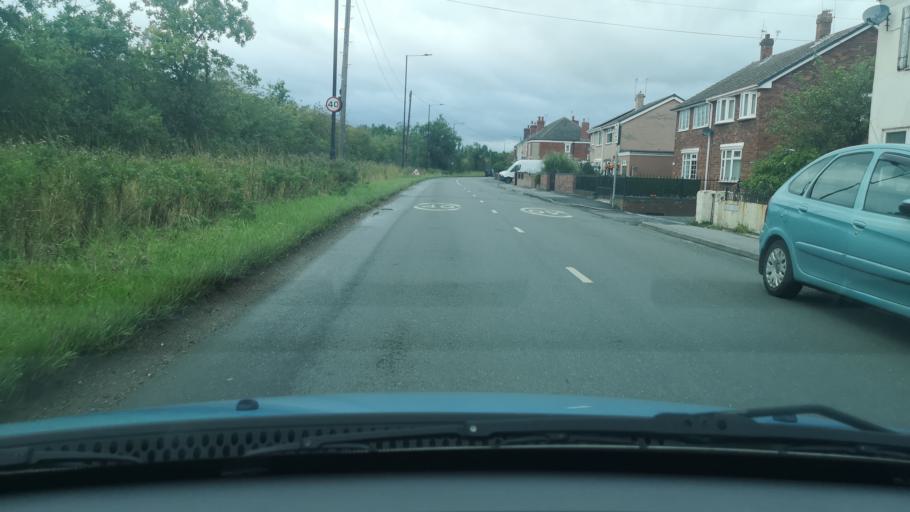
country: GB
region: England
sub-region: Doncaster
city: Hatfield
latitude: 53.5996
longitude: -1.0082
